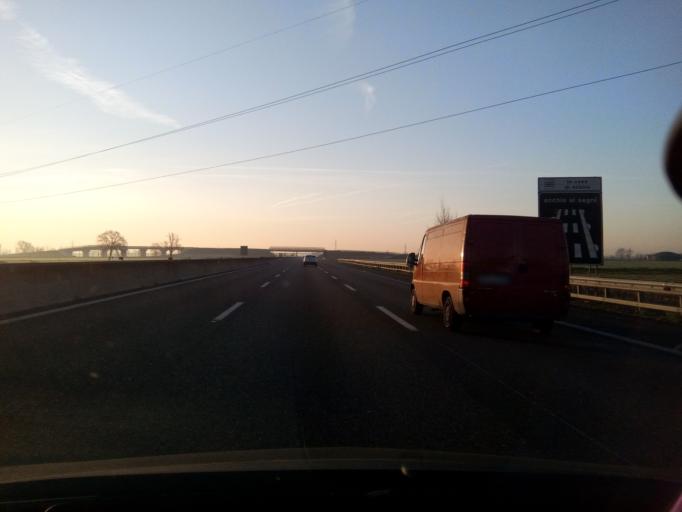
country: IT
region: Lombardy
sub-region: Provincia di Lodi
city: Salerano sul Lambro
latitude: 45.3181
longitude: 9.3810
